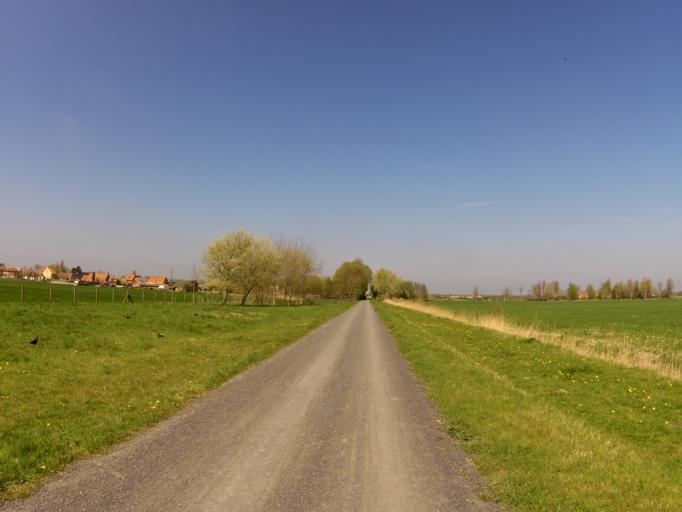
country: BE
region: Flanders
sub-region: Provincie West-Vlaanderen
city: Nieuwpoort
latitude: 51.1083
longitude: 2.7695
